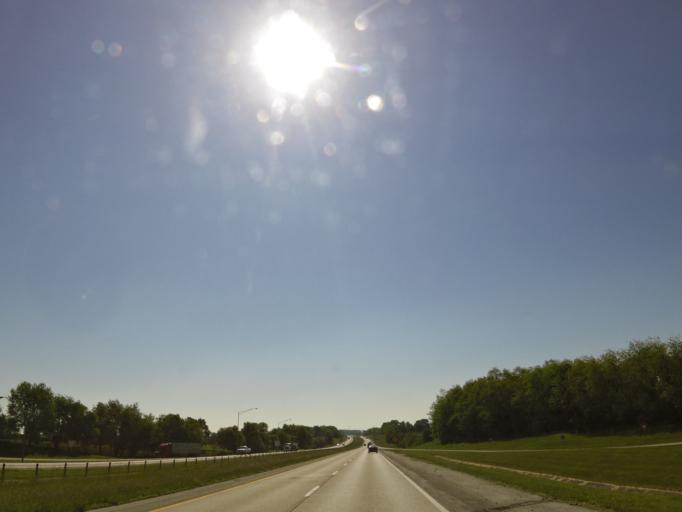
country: US
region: Kentucky
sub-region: Woodford County
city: Midway
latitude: 38.1690
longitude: -84.7647
